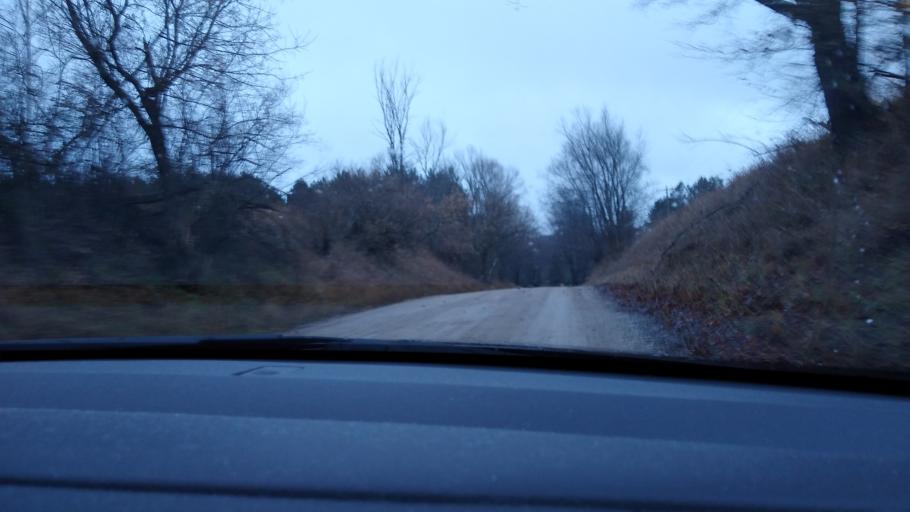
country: US
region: Michigan
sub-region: Wexford County
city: Cadillac
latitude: 44.1675
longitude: -85.3953
